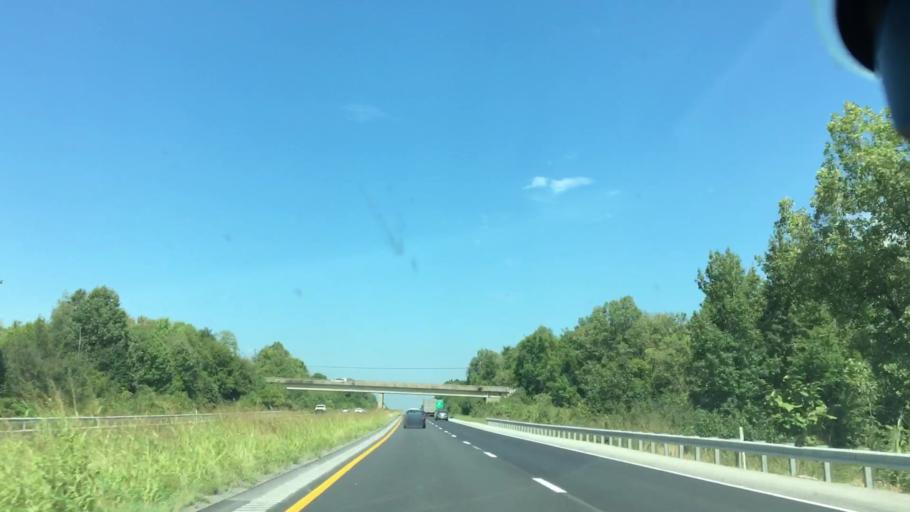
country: US
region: Kentucky
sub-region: Hopkins County
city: Madisonville
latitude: 37.3936
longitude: -87.4763
